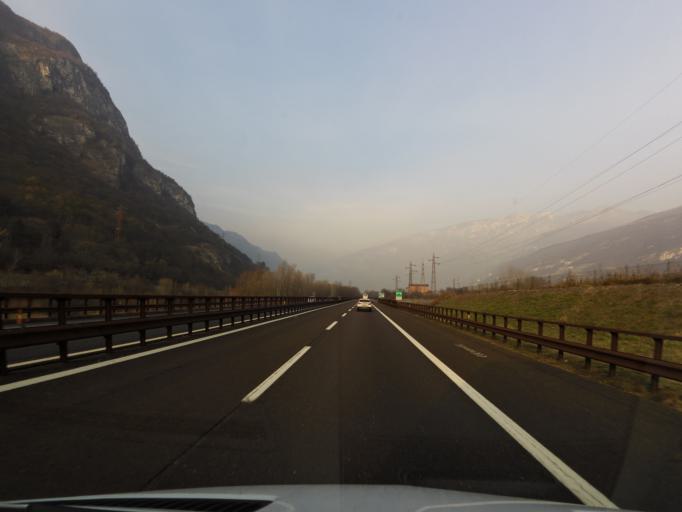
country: IT
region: Trentino-Alto Adige
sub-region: Provincia di Trento
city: Ala
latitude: 45.7606
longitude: 10.9962
